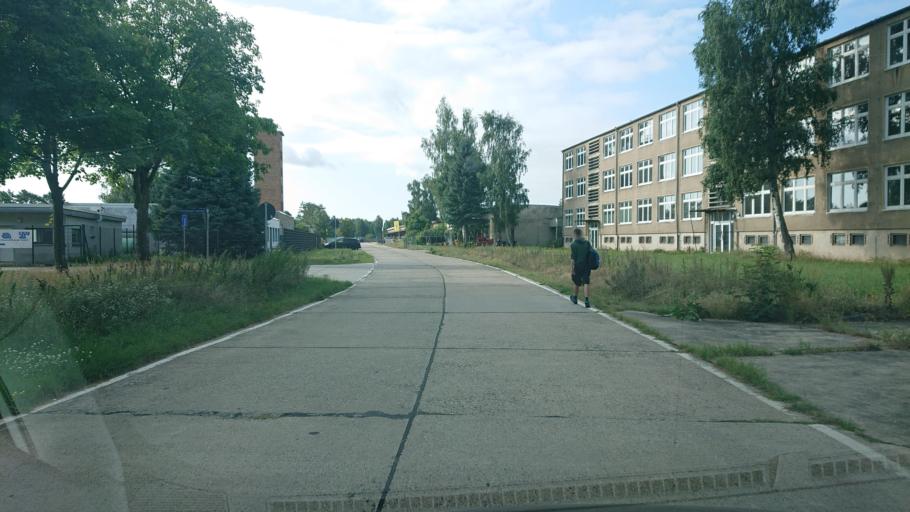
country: DE
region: Brandenburg
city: Gross Kreutz
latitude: 52.3601
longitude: 12.7730
